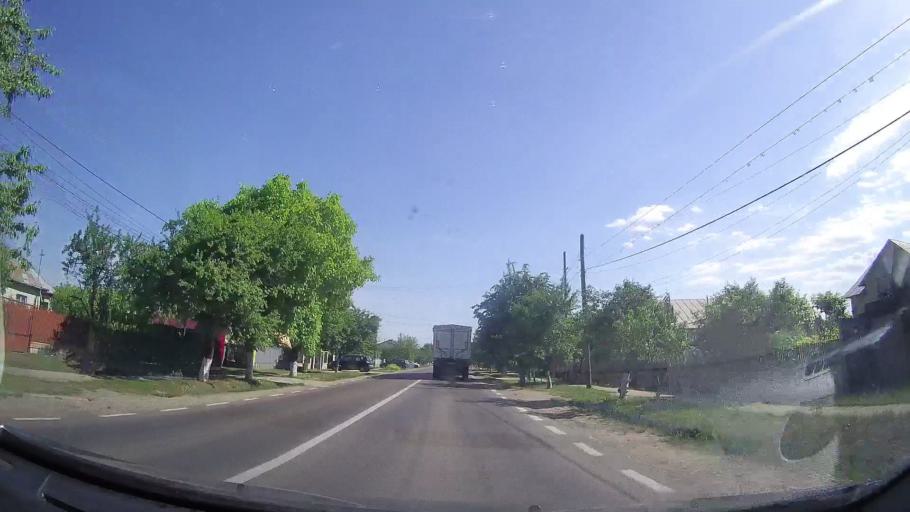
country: RO
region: Prahova
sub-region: Comuna Magurele
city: Magurele
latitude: 45.0927
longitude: 26.0368
